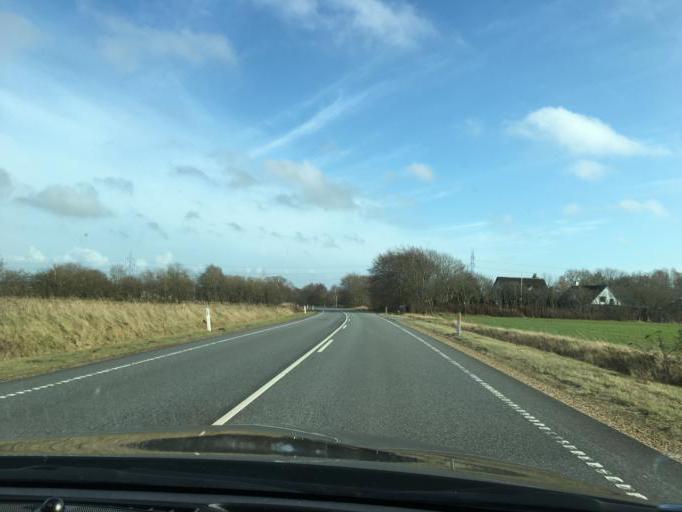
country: DK
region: South Denmark
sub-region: Esbjerg Kommune
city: Tjaereborg
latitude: 55.5076
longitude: 8.5976
